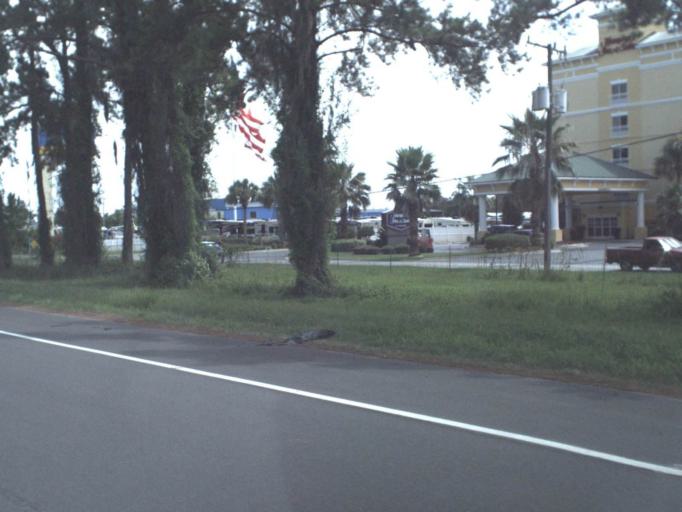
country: US
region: Florida
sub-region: Columbia County
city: Lake City
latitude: 30.1768
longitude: -82.6872
